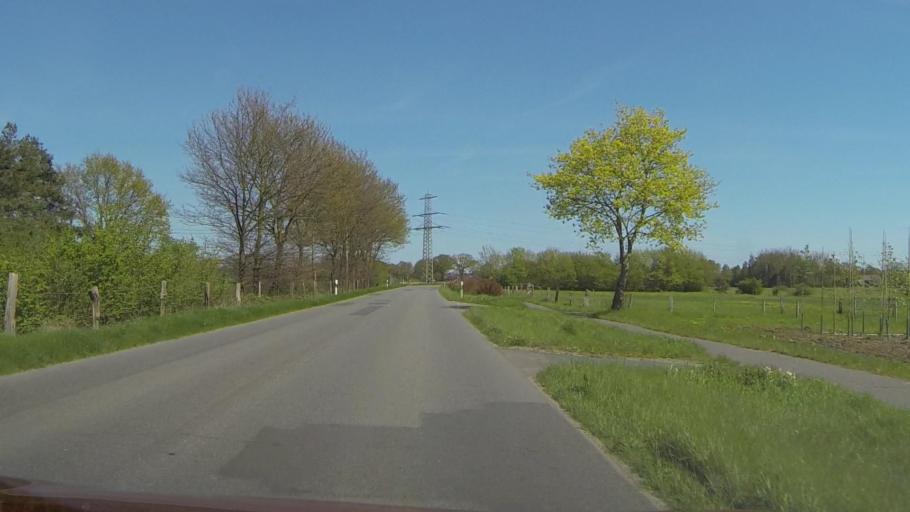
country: DE
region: Schleswig-Holstein
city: Tangstedt
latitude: 53.6616
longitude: 9.8535
